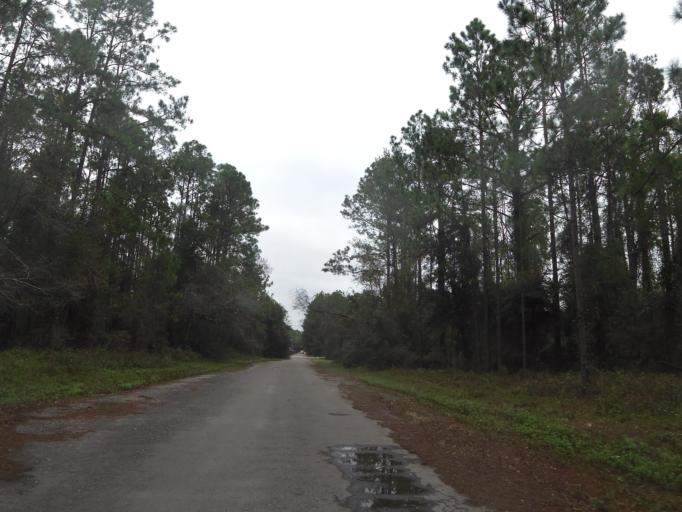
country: US
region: Florida
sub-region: Duval County
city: Baldwin
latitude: 30.2219
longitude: -81.8959
